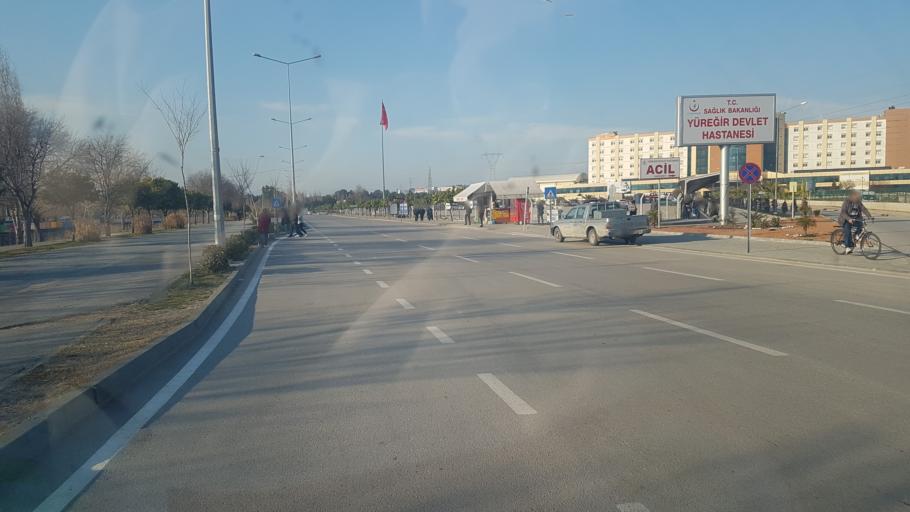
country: TR
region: Adana
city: Adana
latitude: 37.0083
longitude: 35.3540
